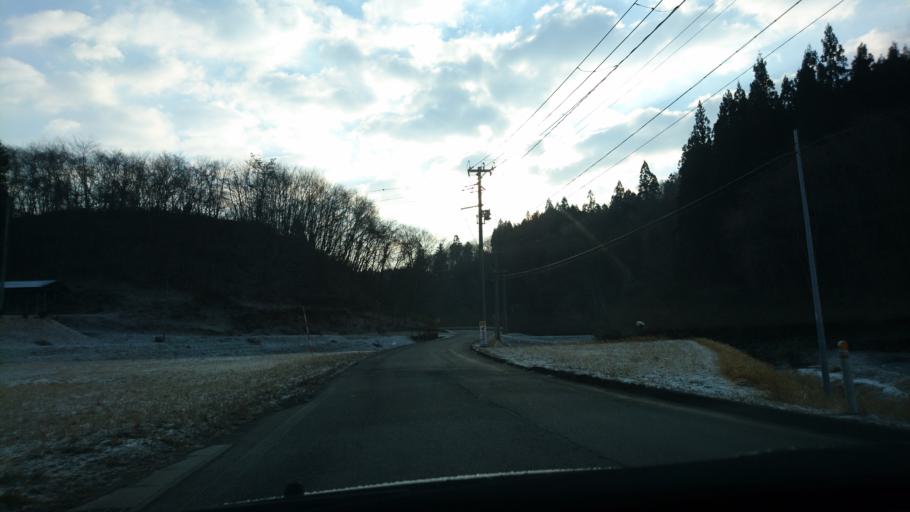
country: JP
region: Iwate
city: Ichinoseki
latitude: 38.9192
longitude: 141.3544
